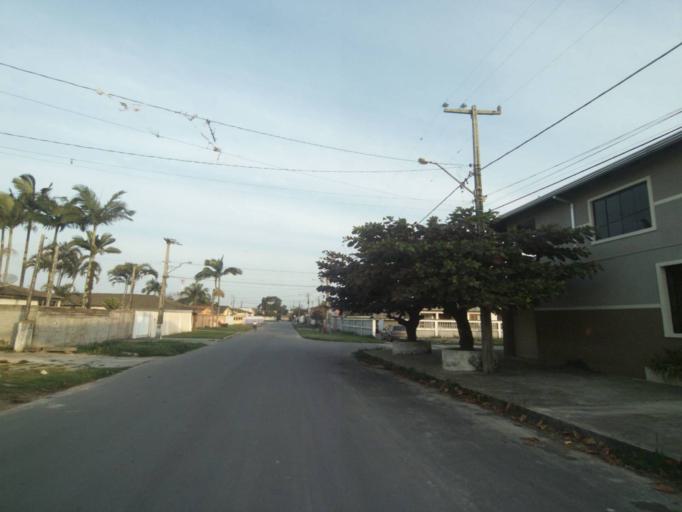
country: BR
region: Parana
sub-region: Paranagua
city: Paranagua
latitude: -25.5132
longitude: -48.5406
